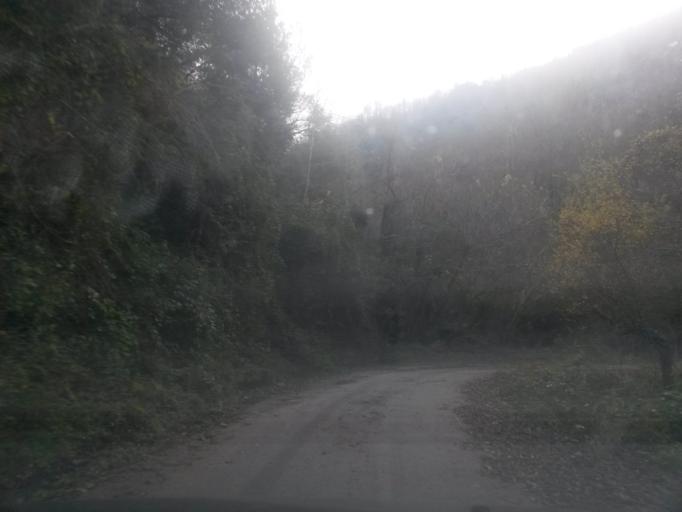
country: ES
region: Catalonia
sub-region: Provincia de Girona
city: Susqueda
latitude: 41.9701
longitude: 2.5251
